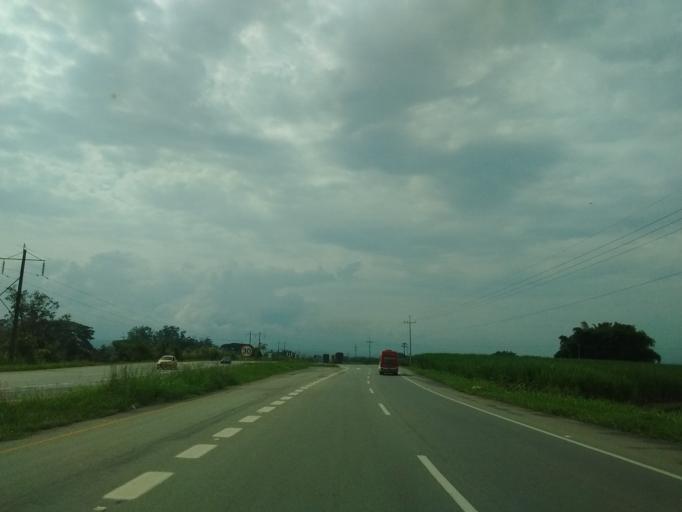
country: CO
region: Cauca
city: Santander de Quilichao
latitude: 3.0738
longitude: -76.4754
